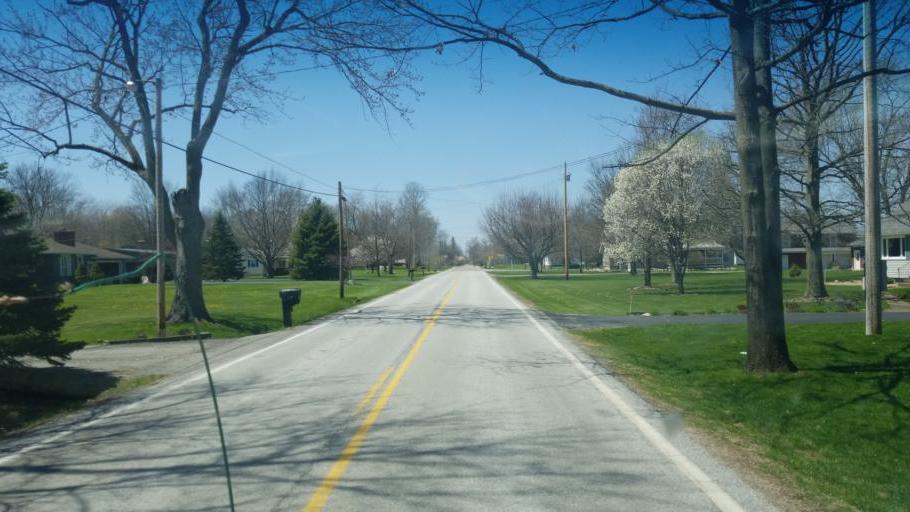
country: US
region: Ohio
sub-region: Huron County
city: New London
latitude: 41.0841
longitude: -82.3839
